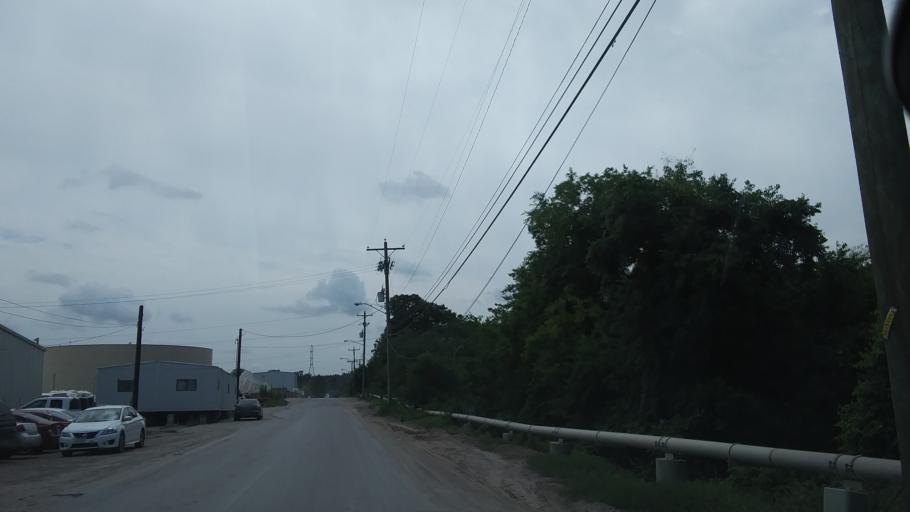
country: US
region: Tennessee
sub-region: Davidson County
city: Belle Meade
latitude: 36.1615
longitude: -86.8846
